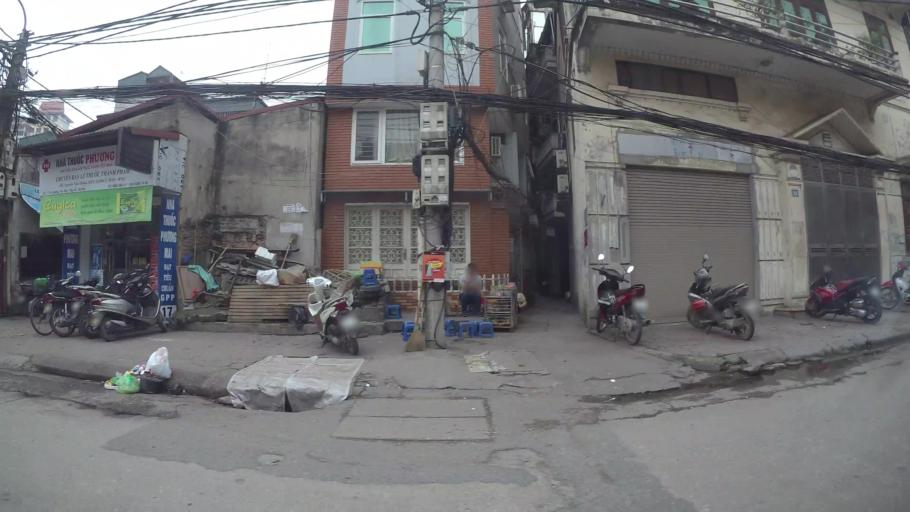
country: VN
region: Ha Noi
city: Hoan Kiem
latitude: 21.0519
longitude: 105.8408
